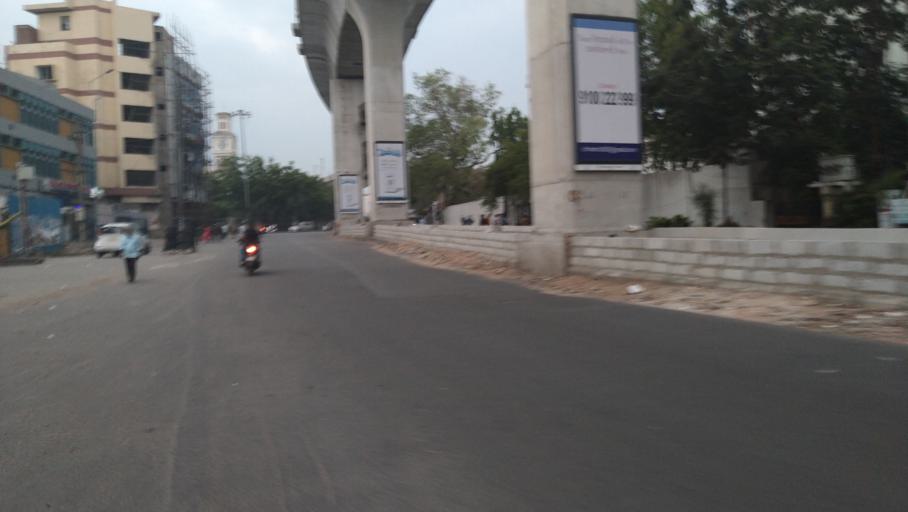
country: IN
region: Telangana
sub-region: Hyderabad
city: Malkajgiri
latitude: 17.4395
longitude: 78.4989
